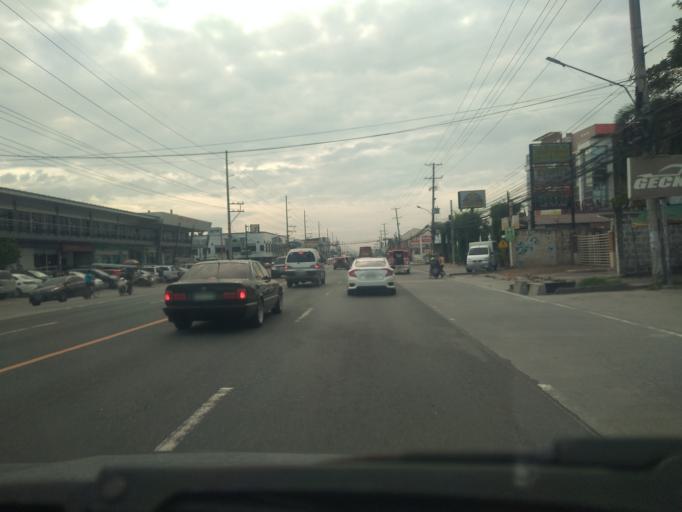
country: PH
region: Central Luzon
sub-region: Province of Pampanga
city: Bulaon
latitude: 15.0687
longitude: 120.6485
